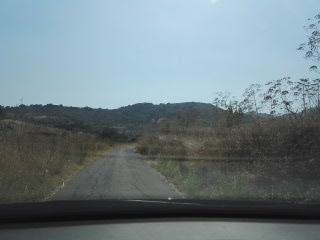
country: IT
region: Calabria
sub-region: Provincia di Reggio Calabria
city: Camini
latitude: 38.4406
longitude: 16.4642
